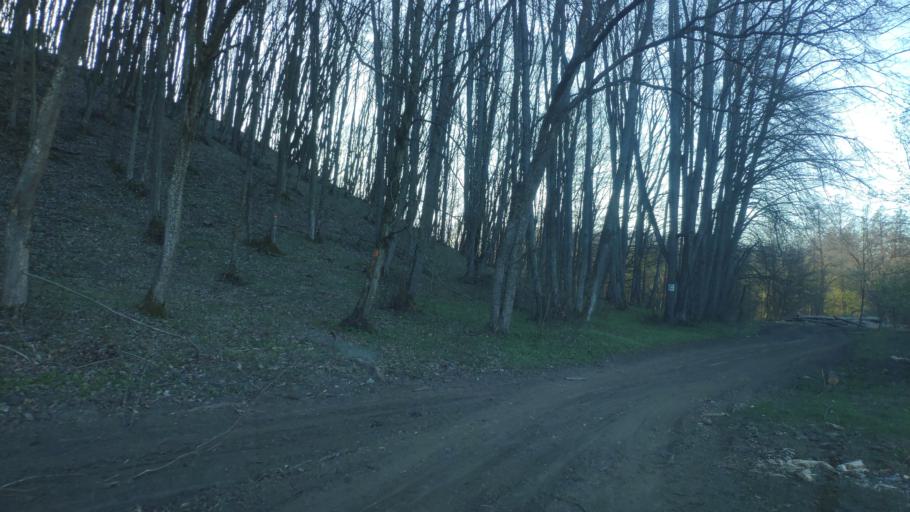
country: HU
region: Borsod-Abauj-Zemplen
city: Putnok
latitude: 48.5201
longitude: 20.3105
